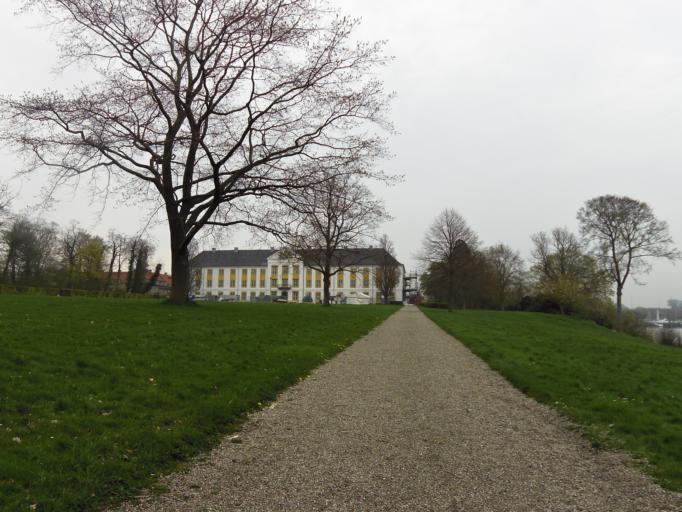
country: DK
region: South Denmark
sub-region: Sonderborg Kommune
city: Augustenborg
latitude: 54.9438
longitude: 9.8640
